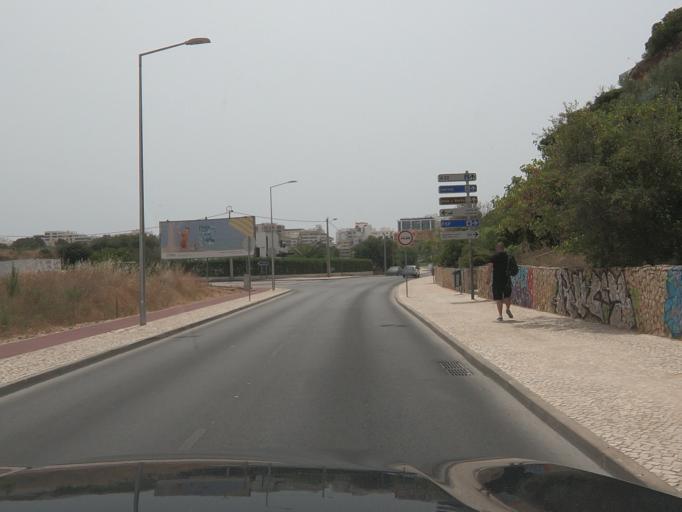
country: PT
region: Faro
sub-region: Portimao
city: Portimao
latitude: 37.1247
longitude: -8.5347
